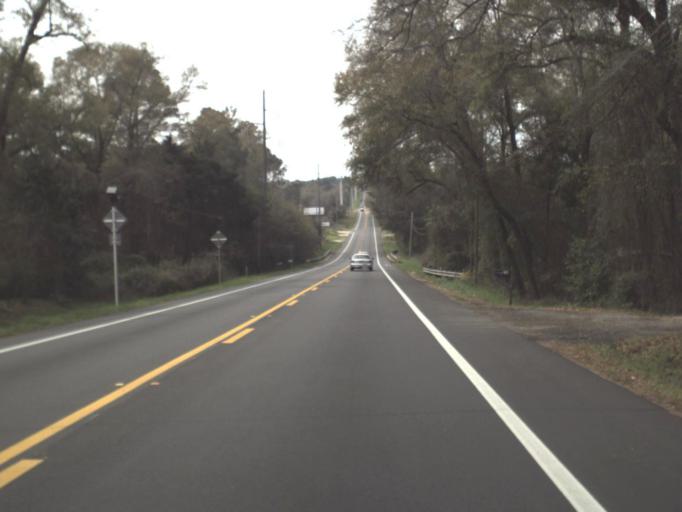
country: US
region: Florida
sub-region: Leon County
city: Tallahassee
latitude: 30.4351
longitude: -84.3661
